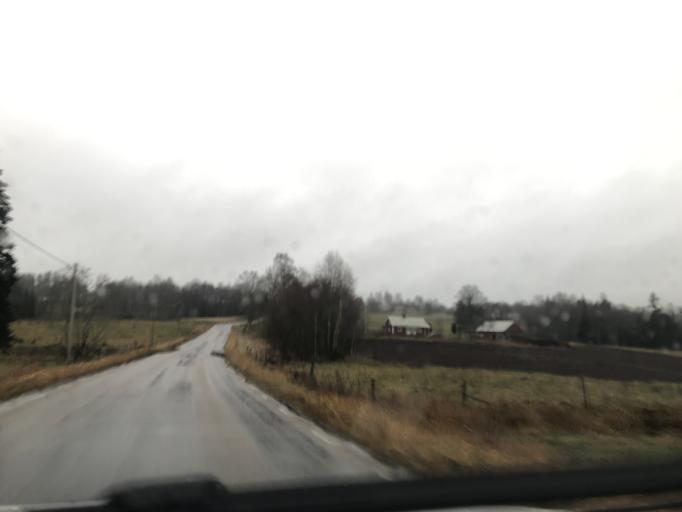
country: SE
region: Vaestra Goetaland
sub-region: Ulricehamns Kommun
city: Ulricehamn
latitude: 57.8541
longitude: 13.5481
